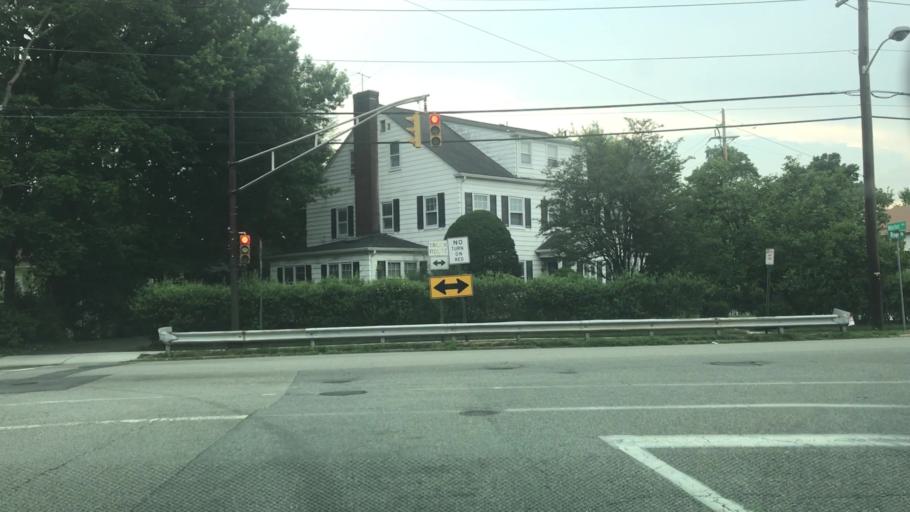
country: US
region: New Jersey
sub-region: Bergen County
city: Fair Lawn
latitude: 40.9268
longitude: -74.1296
